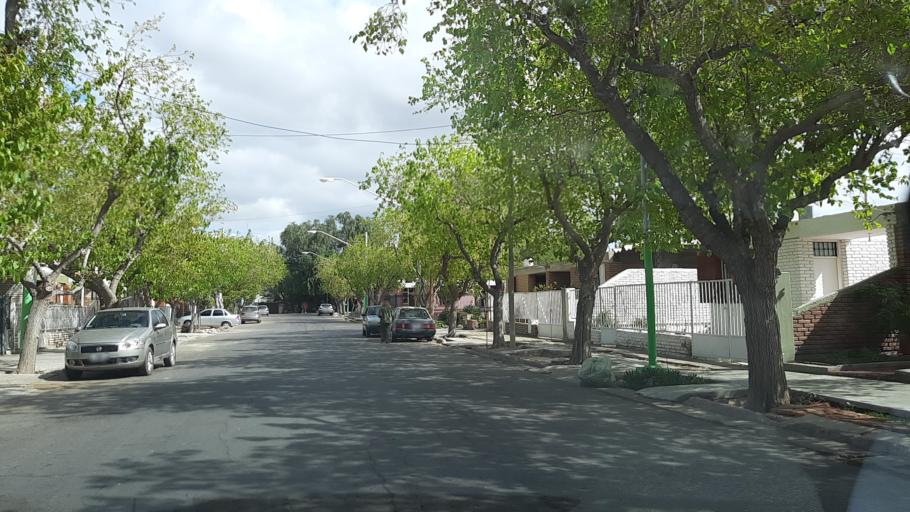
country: AR
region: San Juan
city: San Juan
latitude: -31.5316
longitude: -68.5903
